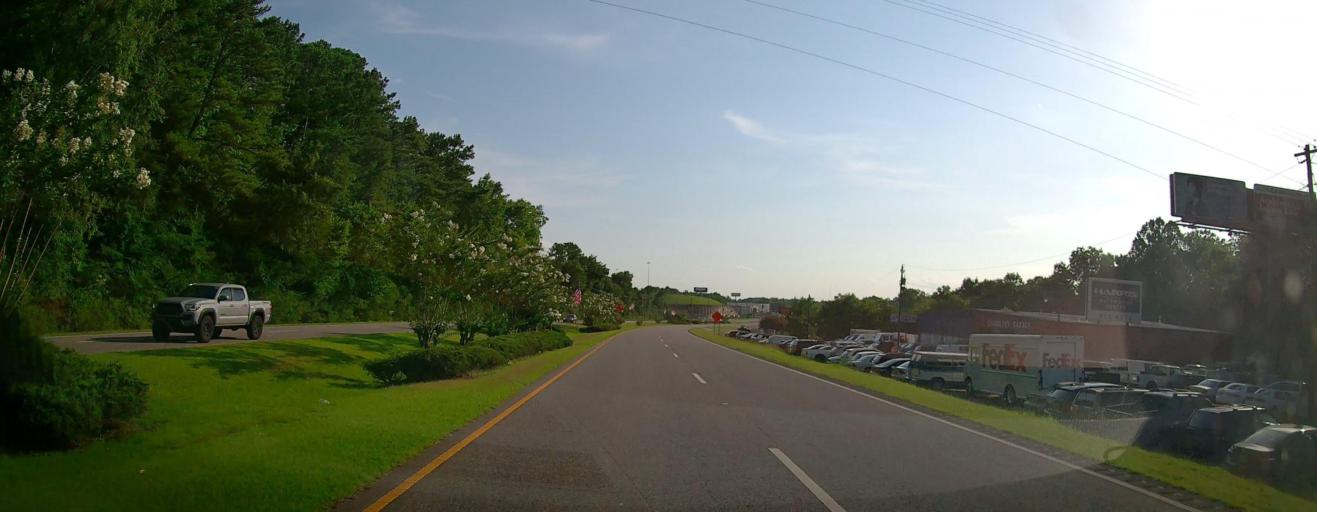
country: US
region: Alabama
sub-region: Jefferson County
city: Irondale
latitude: 33.5380
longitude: -86.6939
